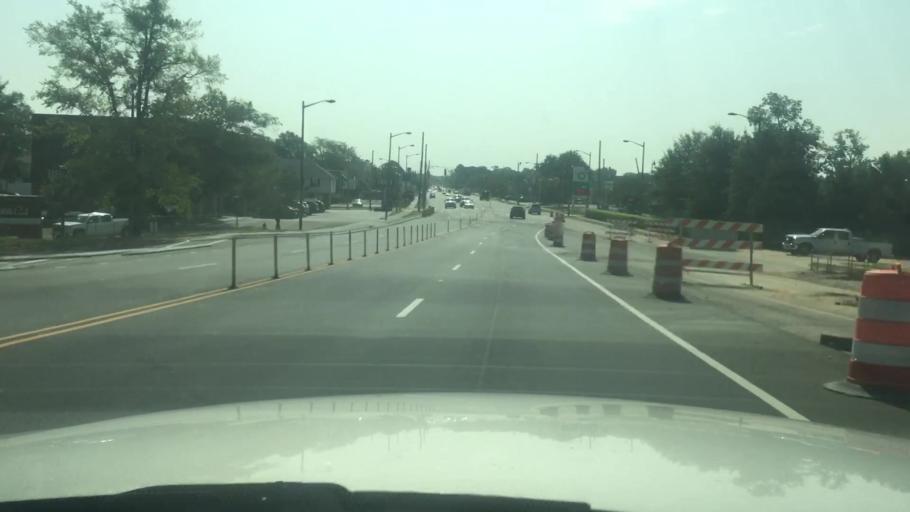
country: US
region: North Carolina
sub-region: Cumberland County
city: Fayetteville
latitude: 35.0591
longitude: -78.8818
